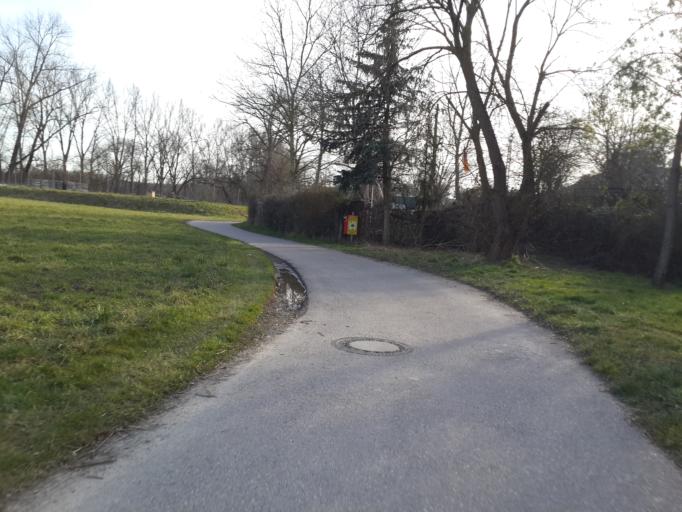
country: DE
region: Baden-Wuerttemberg
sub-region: Regierungsbezirk Stuttgart
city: Nordheim
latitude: 49.1124
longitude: 9.1512
